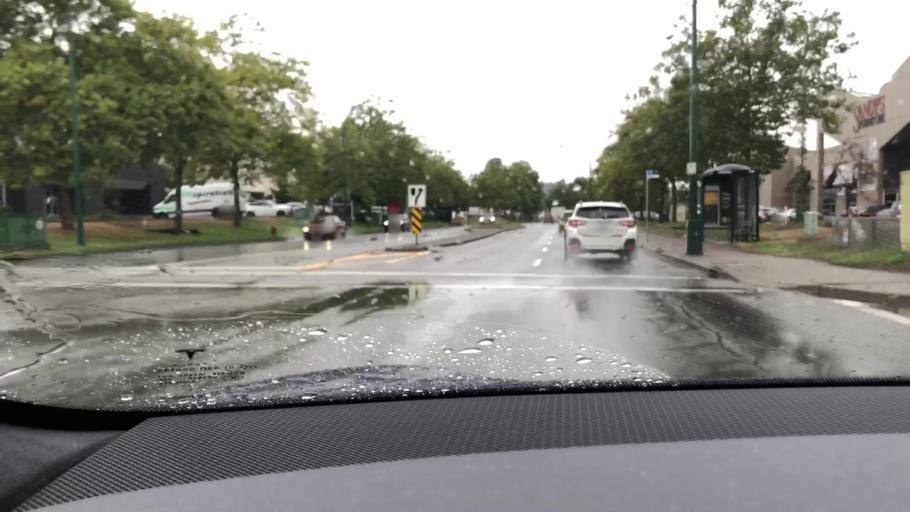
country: CA
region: British Columbia
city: Port Moody
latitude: 49.2294
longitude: -122.8527
